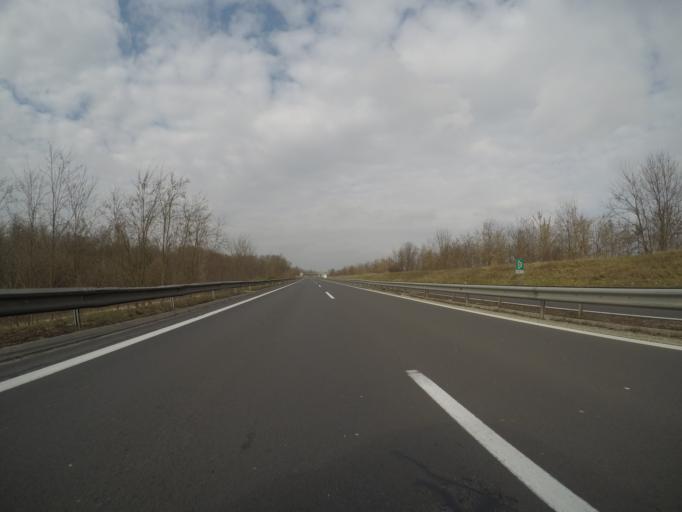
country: SI
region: Murska Sobota
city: Bakovci
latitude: 46.6115
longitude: 16.1302
